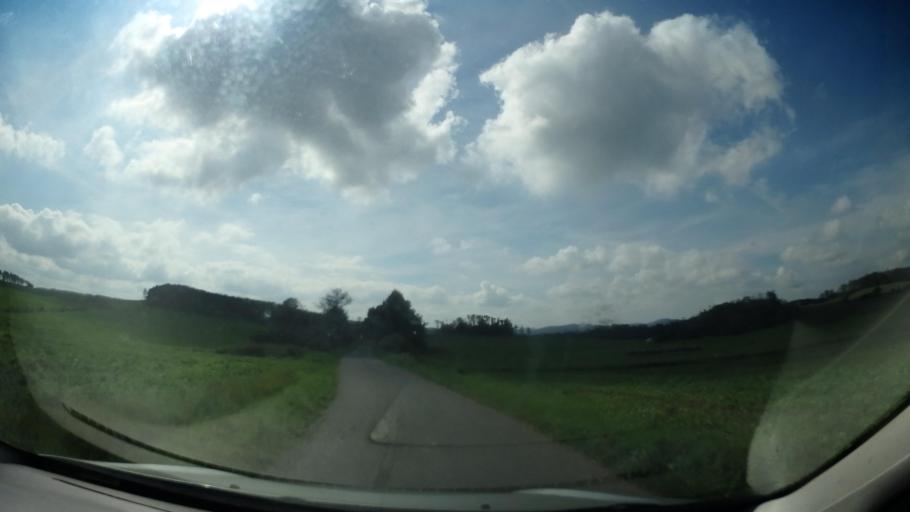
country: CZ
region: Central Bohemia
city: Novy Knin
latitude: 49.7019
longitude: 14.3343
